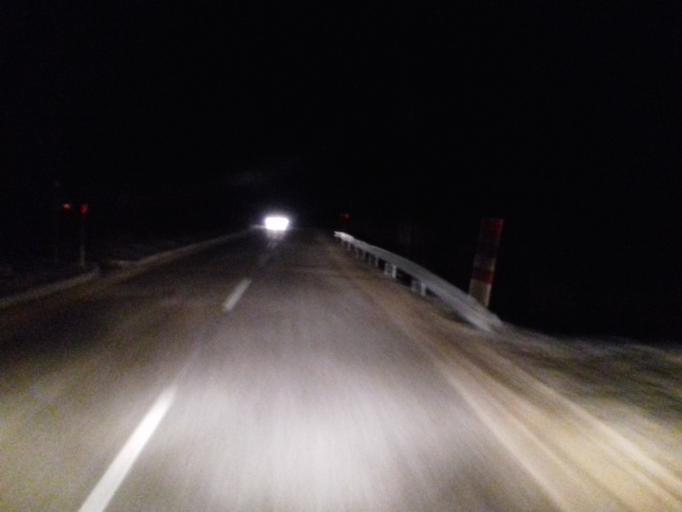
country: BA
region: Federation of Bosnia and Herzegovina
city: Gracanica
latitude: 43.7325
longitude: 18.3135
